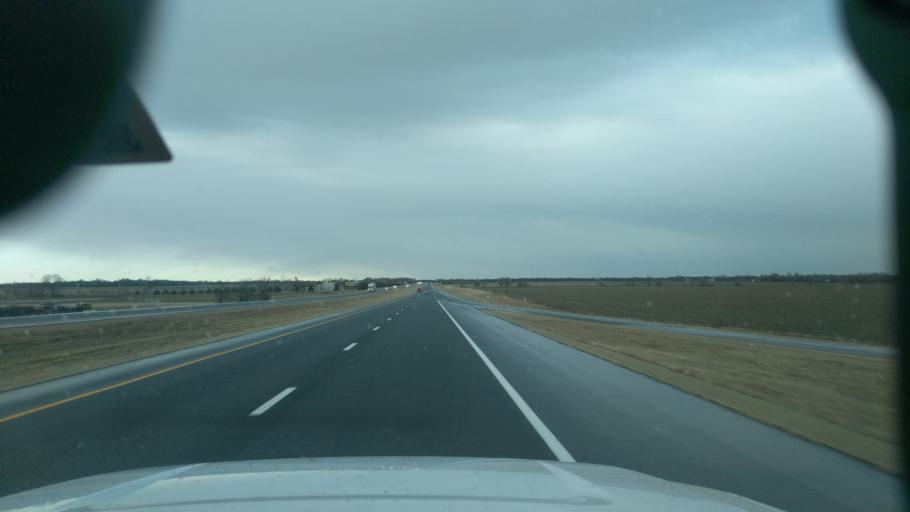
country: US
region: Kansas
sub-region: Harvey County
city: Newton
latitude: 37.9574
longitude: -97.3275
